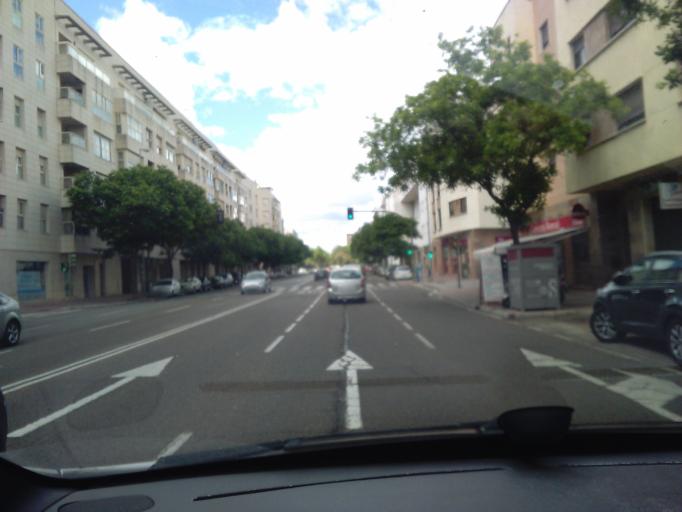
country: ES
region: Andalusia
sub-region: Provincia de Sevilla
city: Sevilla
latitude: 37.3705
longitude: -5.9775
